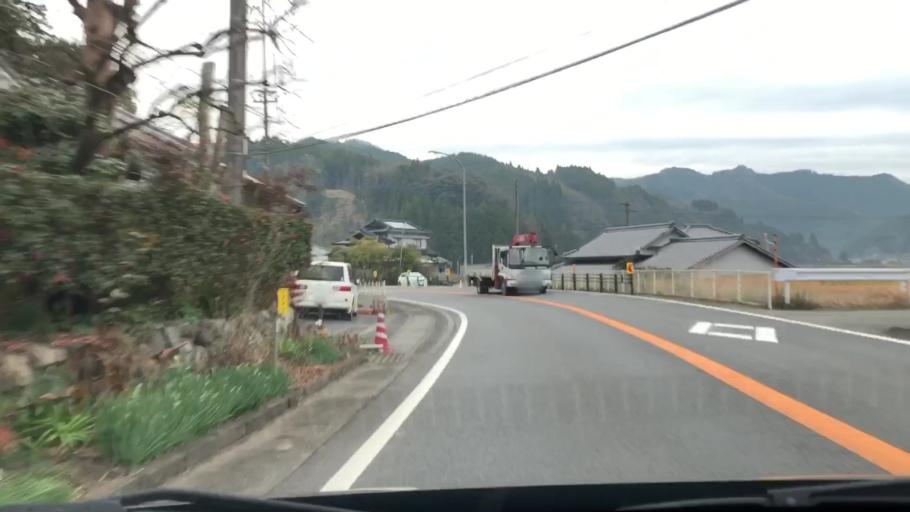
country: JP
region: Oita
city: Usuki
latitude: 33.0076
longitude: 131.7084
